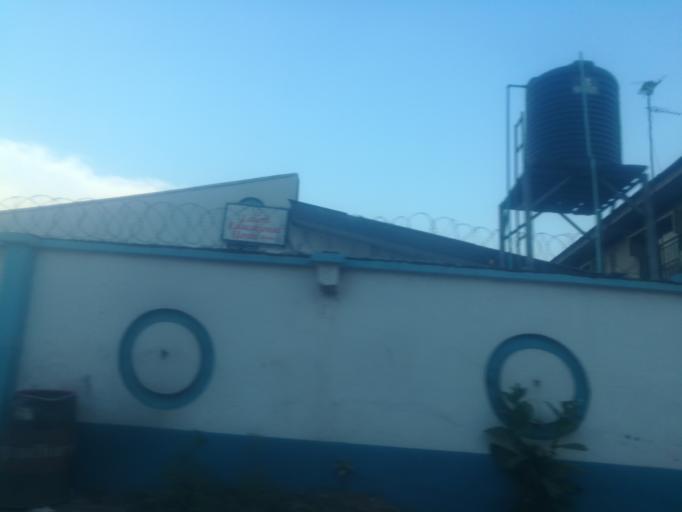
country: NG
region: Oyo
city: Ibadan
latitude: 7.4447
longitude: 3.9198
